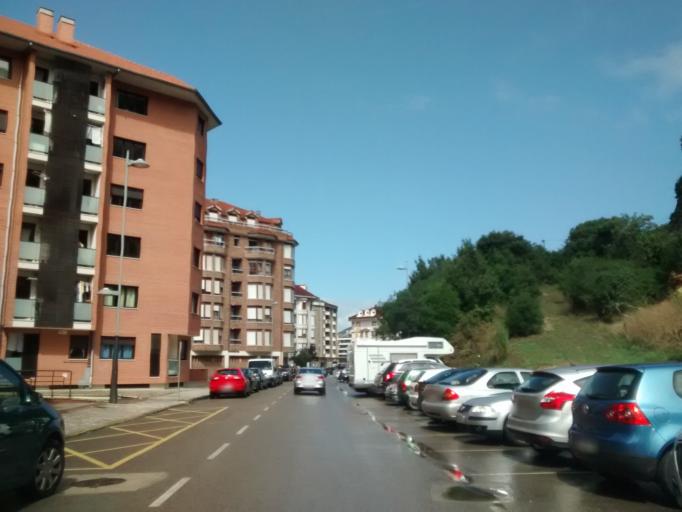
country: ES
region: Cantabria
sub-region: Provincia de Cantabria
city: Santona
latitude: 43.4442
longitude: -3.4521
